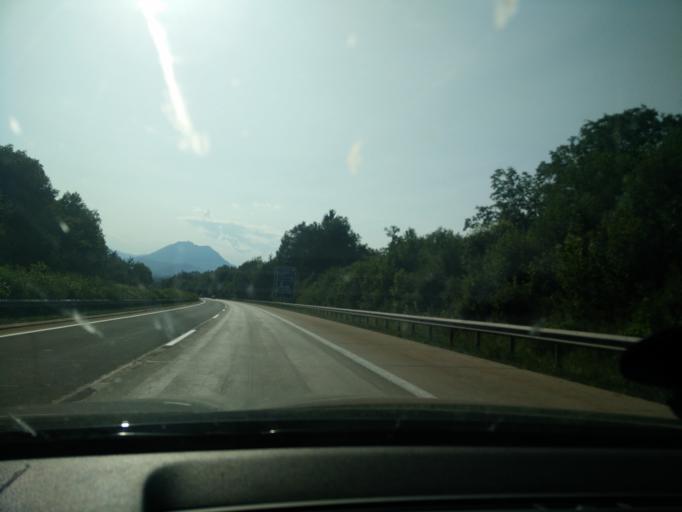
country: AT
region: Carinthia
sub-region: Politischer Bezirk Villach Land
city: Wernberg
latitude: 46.6236
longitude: 13.9293
